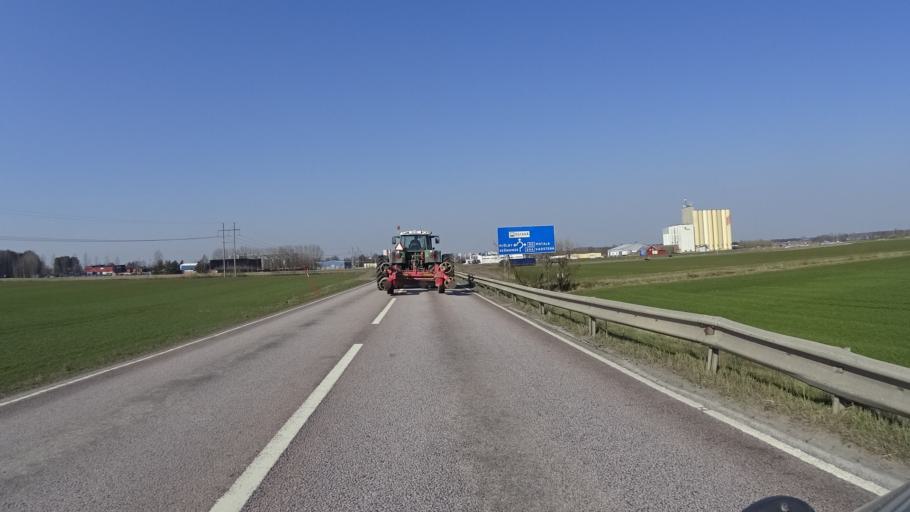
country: SE
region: OEstergoetland
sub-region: Mjolby Kommun
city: Mjolby
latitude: 58.3924
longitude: 15.1098
